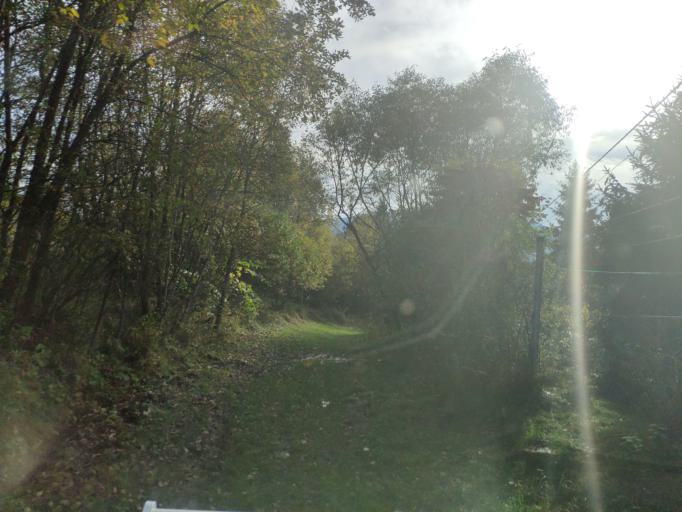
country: SK
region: Presovsky
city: Spisske Podhradie
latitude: 48.8203
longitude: 20.7143
